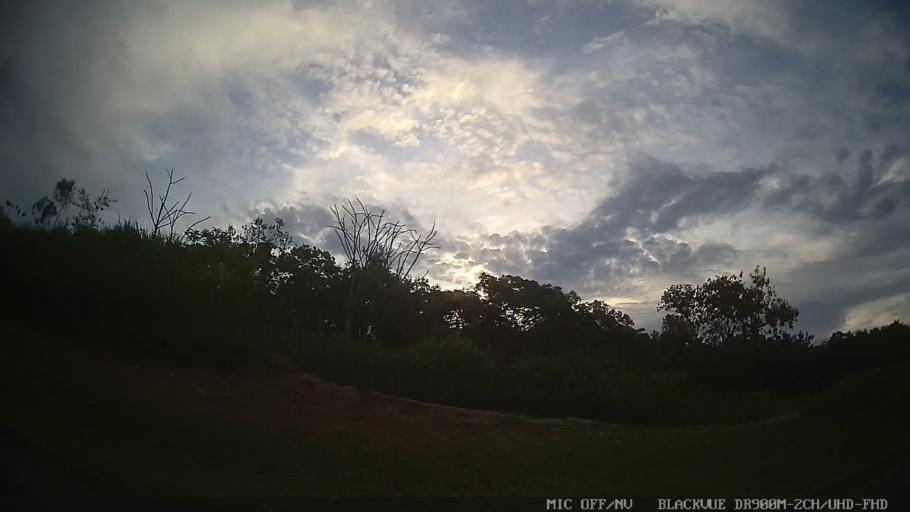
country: BR
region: Sao Paulo
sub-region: Itu
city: Itu
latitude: -23.2587
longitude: -47.2716
